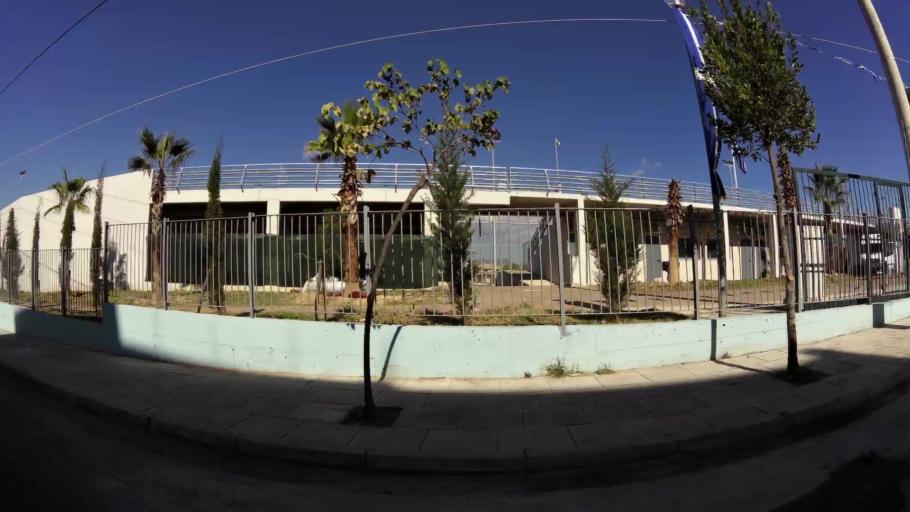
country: GR
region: Attica
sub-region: Nomarchia Athinas
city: Metamorfosi
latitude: 38.0689
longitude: 23.7721
